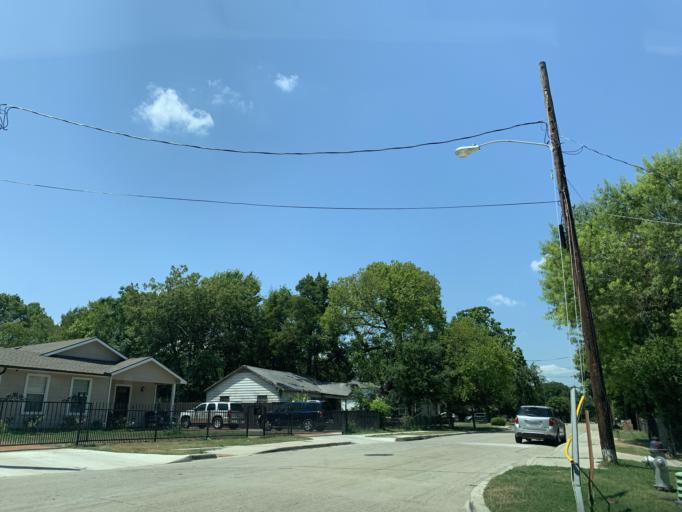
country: US
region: Texas
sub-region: Dallas County
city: Hutchins
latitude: 32.6865
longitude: -96.7739
